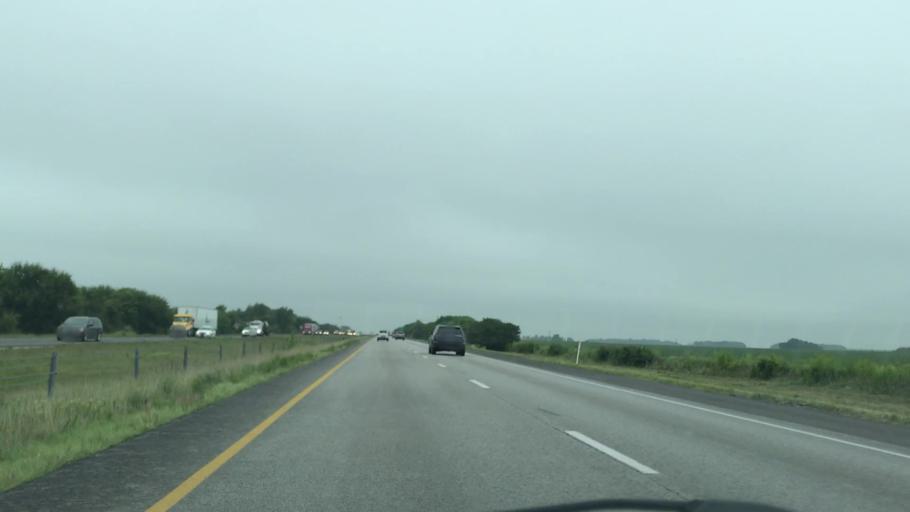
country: US
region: Indiana
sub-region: Clinton County
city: Mulberry
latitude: 40.2463
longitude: -86.6387
